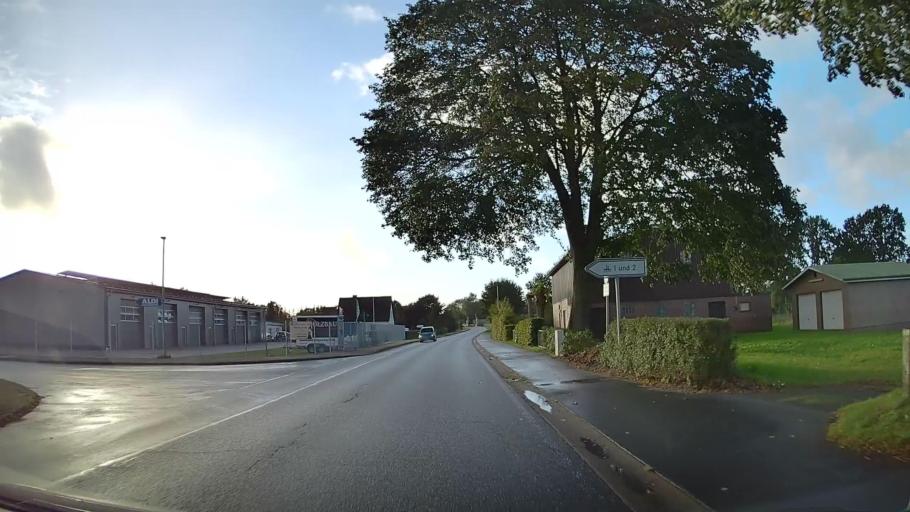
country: DE
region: Schleswig-Holstein
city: Horst
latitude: 53.8047
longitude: 9.6480
